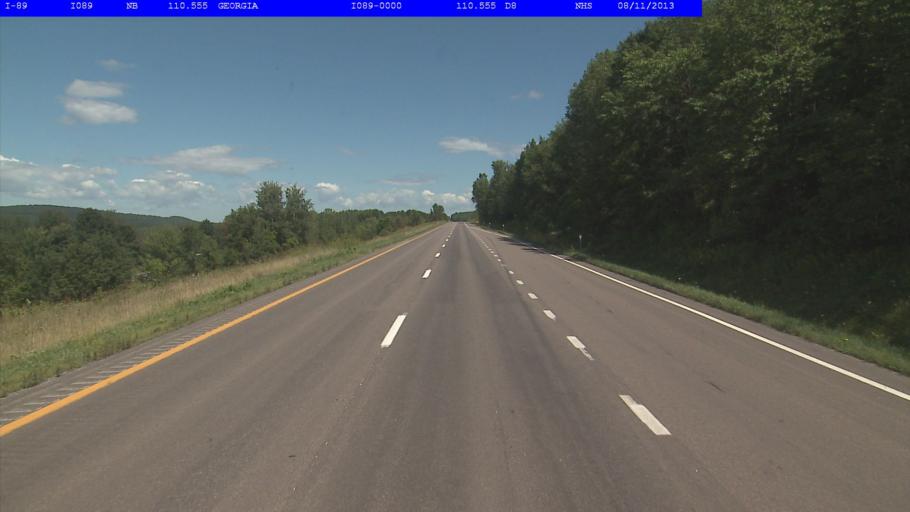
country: US
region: Vermont
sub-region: Franklin County
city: Saint Albans
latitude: 44.7490
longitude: -73.0782
